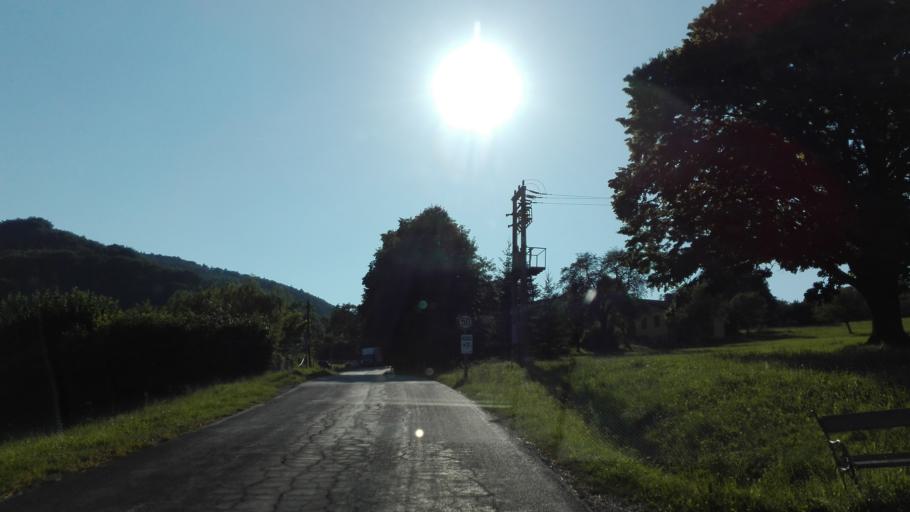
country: AT
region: Lower Austria
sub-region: Politischer Bezirk Sankt Polten
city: Stossing
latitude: 48.0852
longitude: 15.8350
